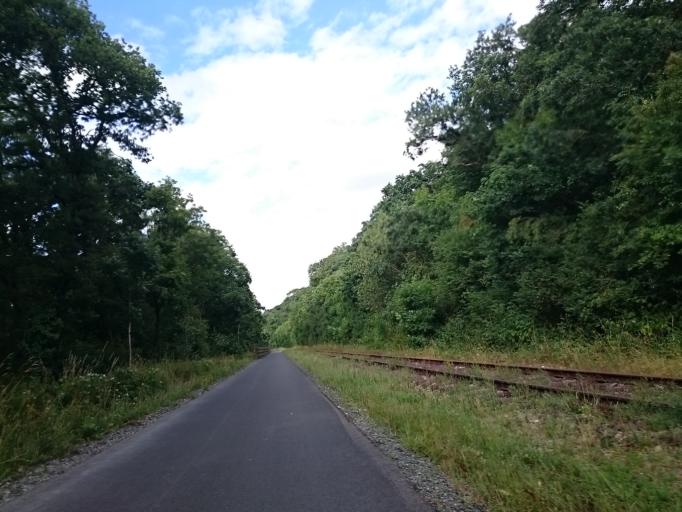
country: FR
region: Lower Normandy
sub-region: Departement du Calvados
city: Clinchamps-sur-Orne
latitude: 49.0666
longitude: -0.4383
